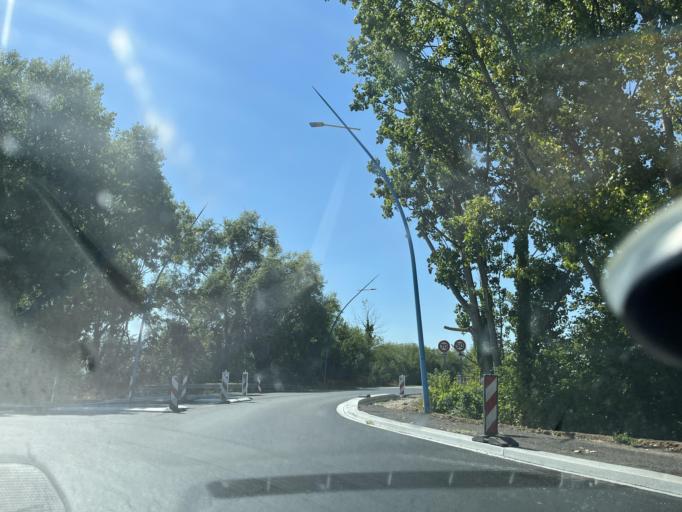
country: FR
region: Haute-Normandie
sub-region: Departement de l'Eure
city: Quillebeuf-sur-Seine
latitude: 49.4856
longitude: 0.5334
